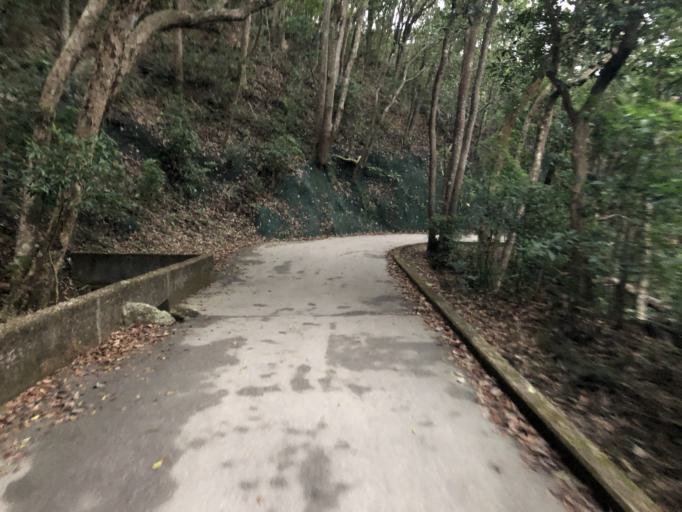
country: HK
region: Wanchai
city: Wan Chai
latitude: 22.2622
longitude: 114.2144
